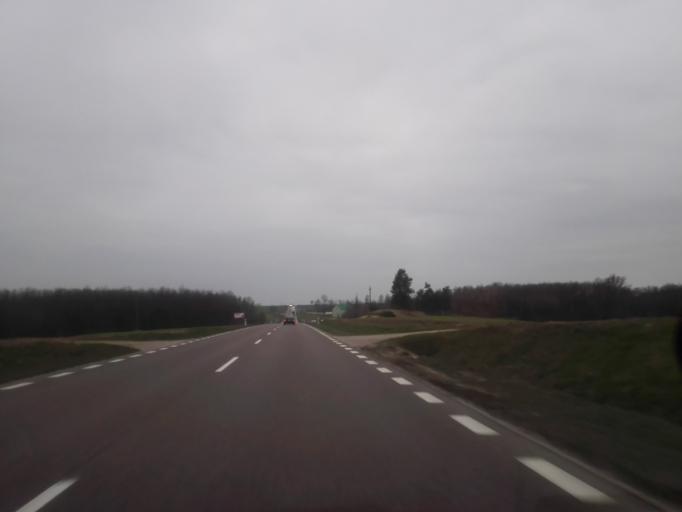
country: PL
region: Podlasie
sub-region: Powiat grajewski
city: Szczuczyn
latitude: 53.5163
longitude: 22.2472
